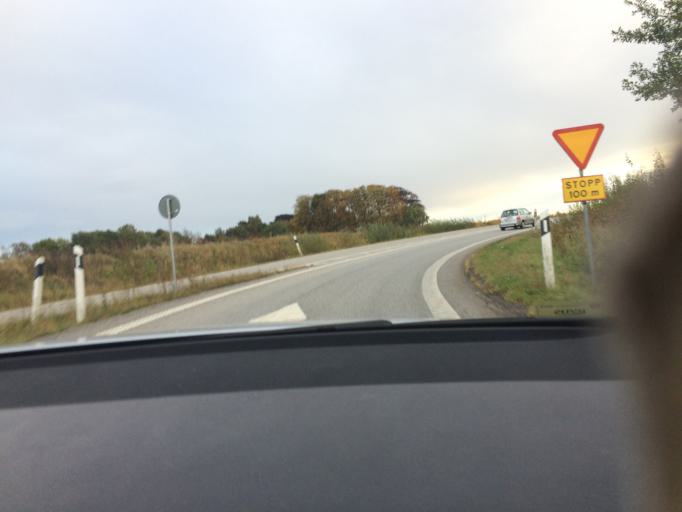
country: SE
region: Skane
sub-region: Hoors Kommun
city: Loberod
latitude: 55.7848
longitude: 13.4185
